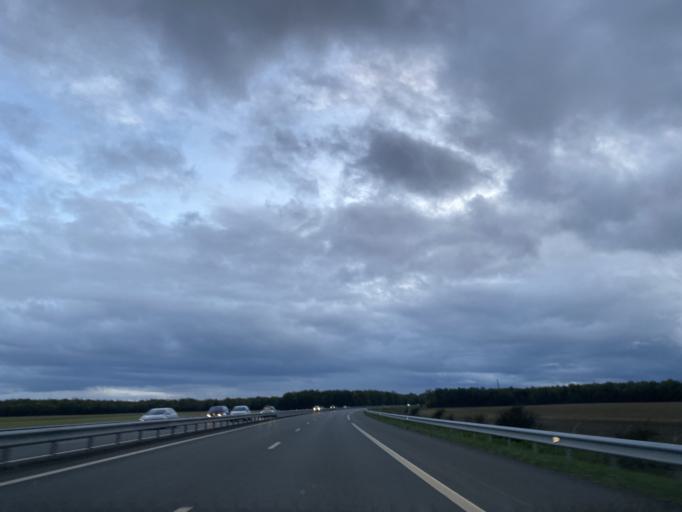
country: FR
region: Centre
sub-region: Departement du Cher
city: Levet
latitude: 46.8562
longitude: 2.4278
